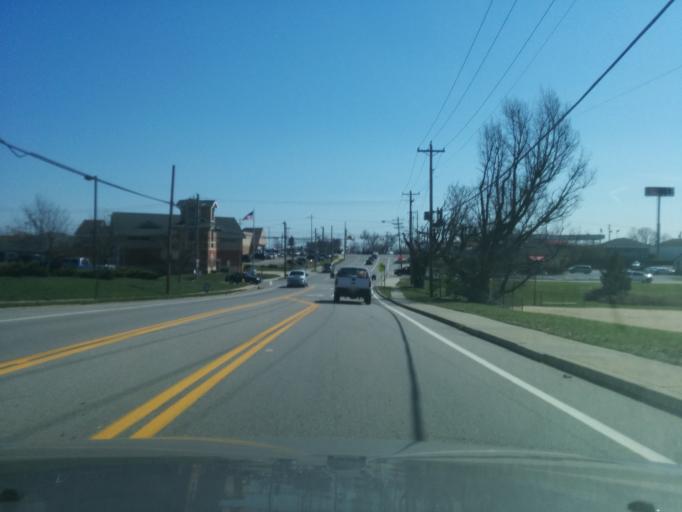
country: US
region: Ohio
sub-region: Hamilton County
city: Monfort Heights
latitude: 39.1891
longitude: -84.6043
